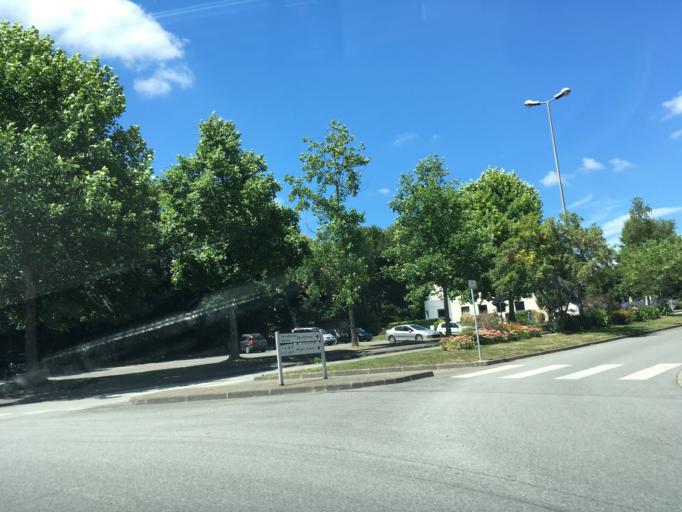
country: FR
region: Brittany
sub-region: Departement du Finistere
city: Quimper
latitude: 47.9757
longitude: -4.0832
